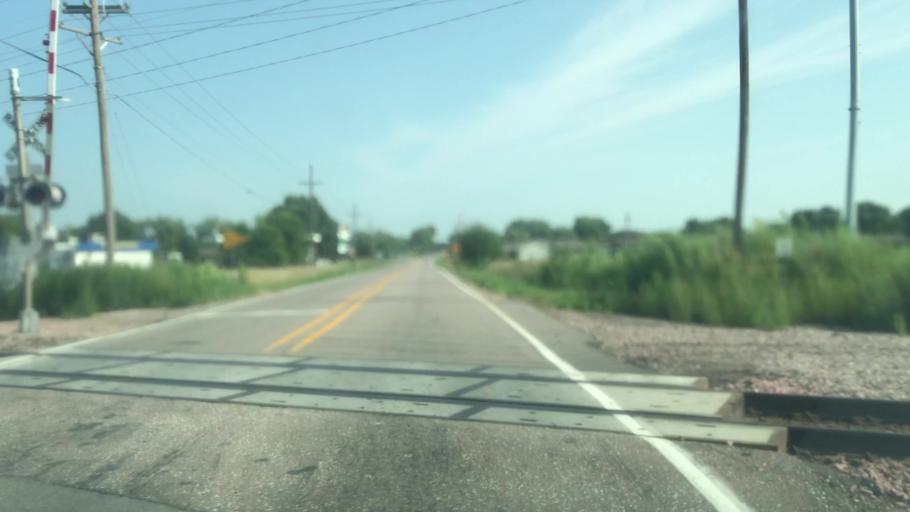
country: US
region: Nebraska
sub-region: Hall County
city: Grand Island
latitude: 40.9140
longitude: -98.3018
